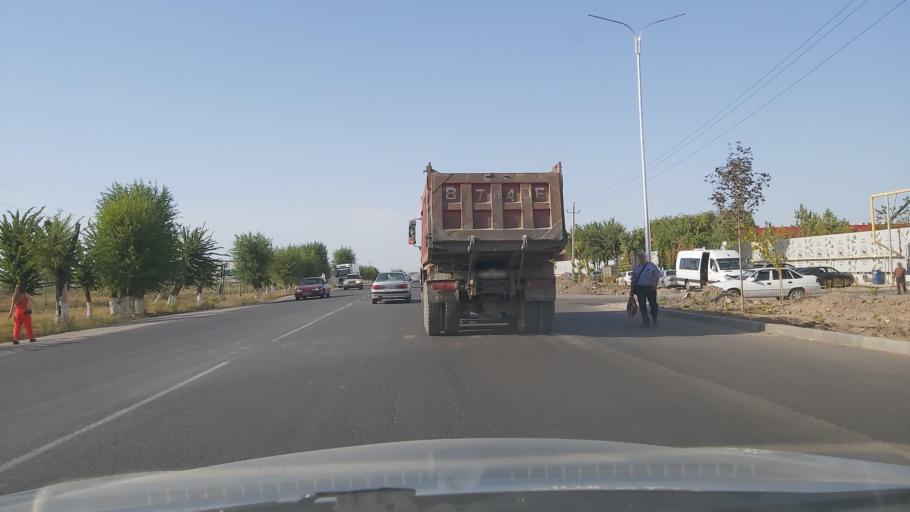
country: KZ
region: Almaty Oblysy
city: Energeticheskiy
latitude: 43.4568
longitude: 77.0340
